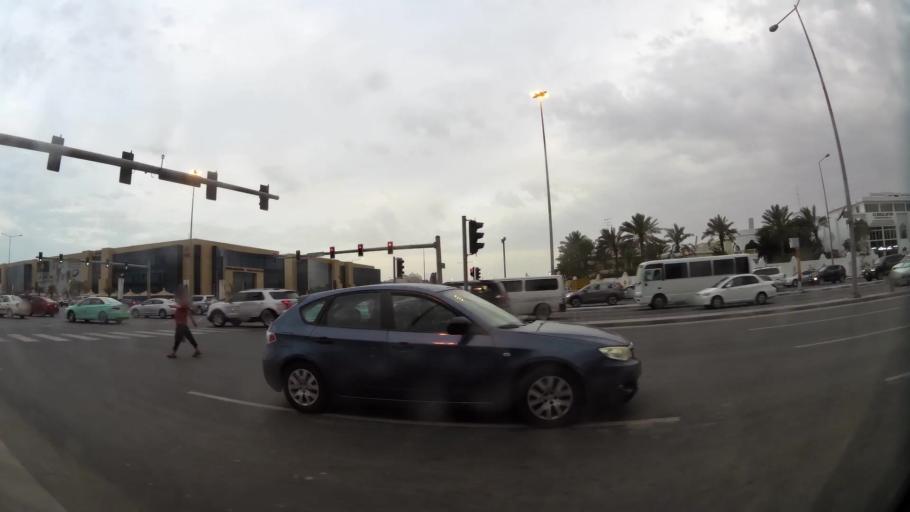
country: QA
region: Baladiyat ad Dawhah
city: Doha
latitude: 25.2633
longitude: 51.5241
